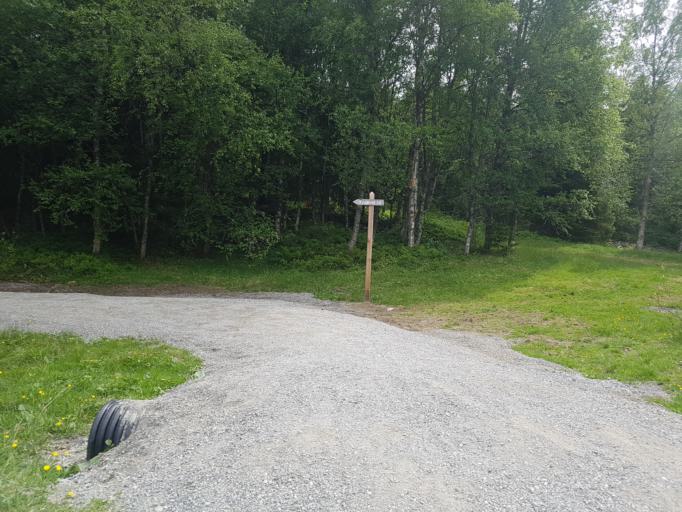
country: NO
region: Sor-Trondelag
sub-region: Trondheim
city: Trondheim
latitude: 63.4163
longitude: 10.3236
